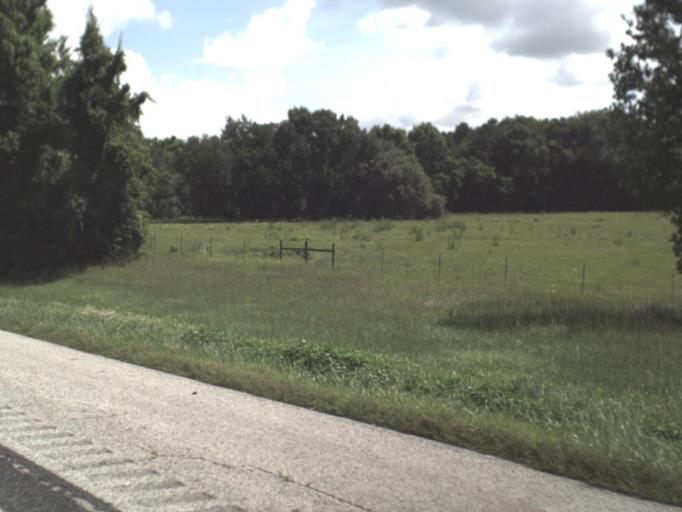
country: US
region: Florida
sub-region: Alachua County
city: High Springs
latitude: 29.7885
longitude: -82.5148
